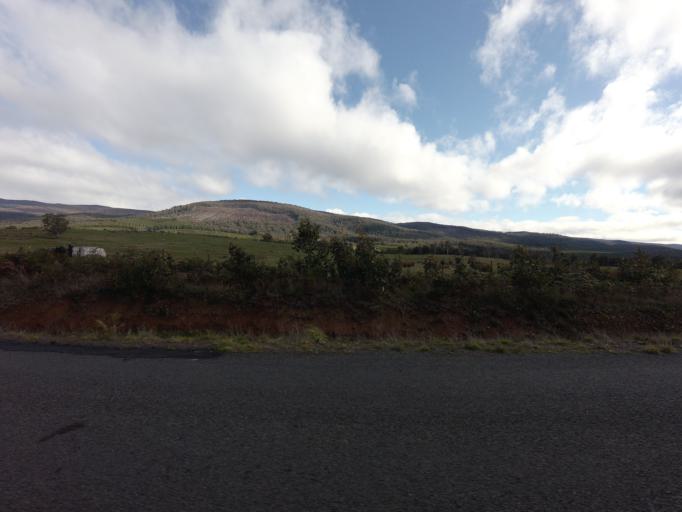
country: AU
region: Tasmania
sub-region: Derwent Valley
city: New Norfolk
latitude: -42.5763
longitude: 146.6981
